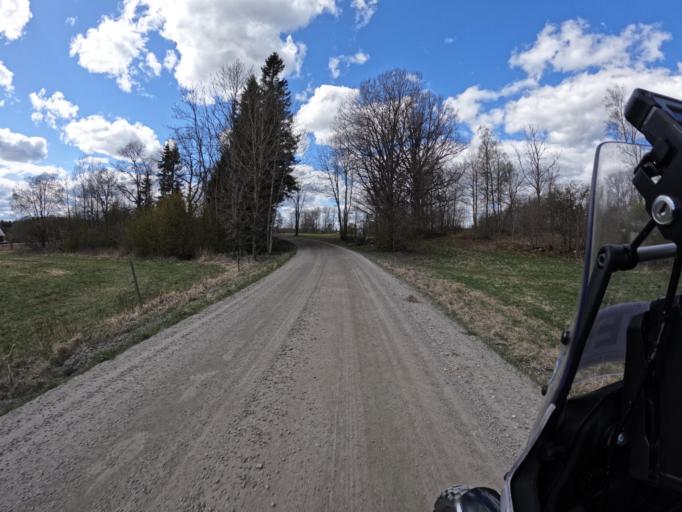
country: SE
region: Vaestra Goetaland
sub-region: Ulricehamns Kommun
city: Ulricehamn
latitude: 57.9305
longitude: 13.2868
